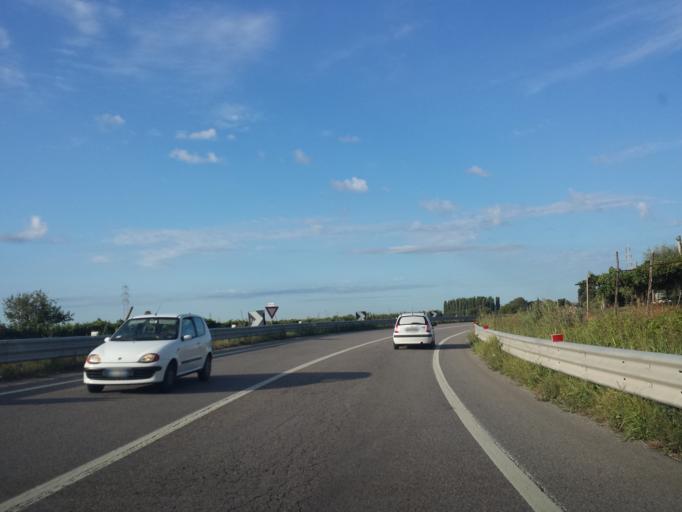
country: IT
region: Veneto
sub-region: Provincia di Verona
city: Soave
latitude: 45.4015
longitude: 11.2526
